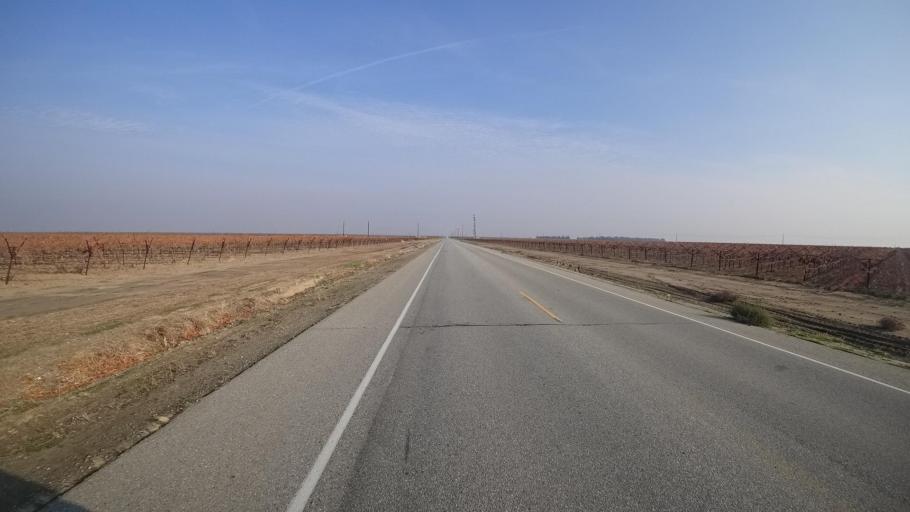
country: US
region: California
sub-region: Kern County
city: Lebec
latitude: 35.0102
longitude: -118.9400
